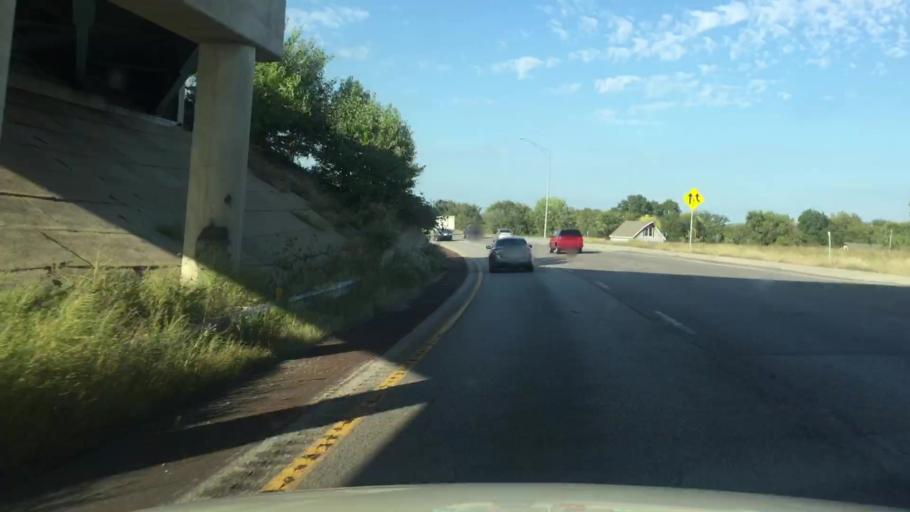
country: US
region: Missouri
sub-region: Jackson County
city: Lees Summit
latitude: 38.9494
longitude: -94.3613
